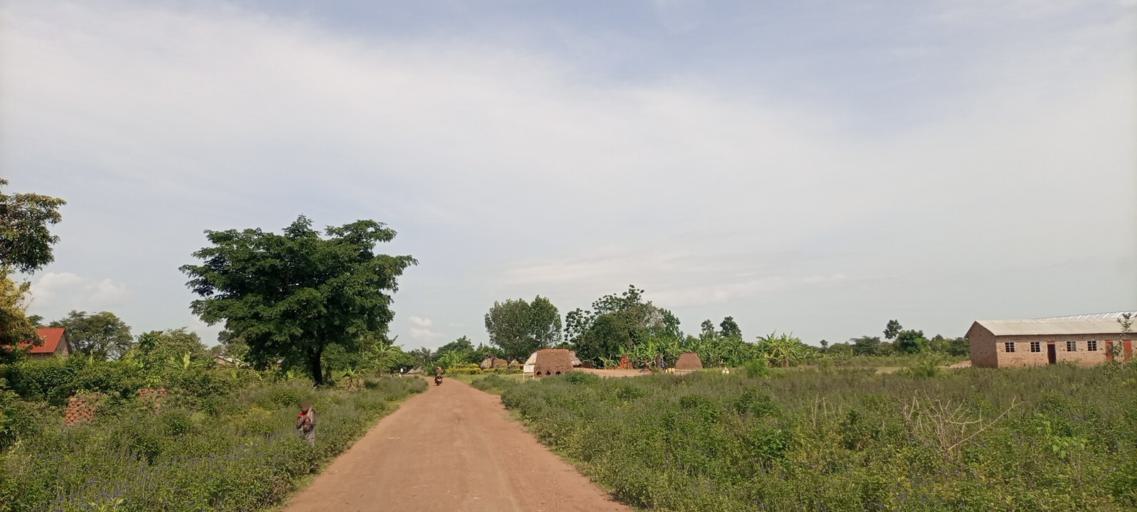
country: UG
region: Eastern Region
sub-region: Mbale District
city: Mbale
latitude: 1.1327
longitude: 34.0507
